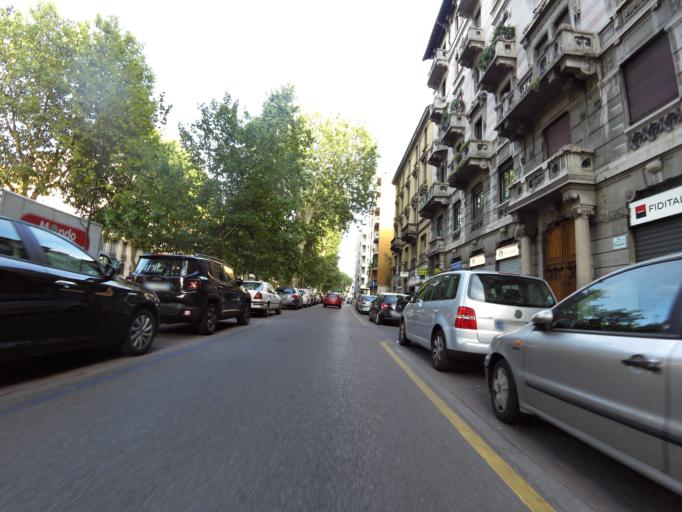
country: IT
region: Lombardy
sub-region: Citta metropolitana di Milano
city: Milano
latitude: 45.4488
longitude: 9.2074
